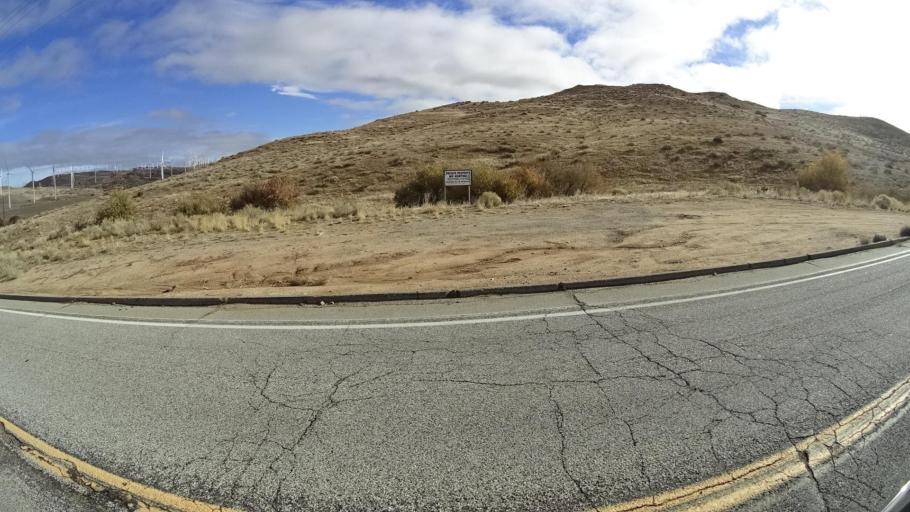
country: US
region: California
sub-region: Kern County
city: Tehachapi
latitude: 35.0470
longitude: -118.3543
